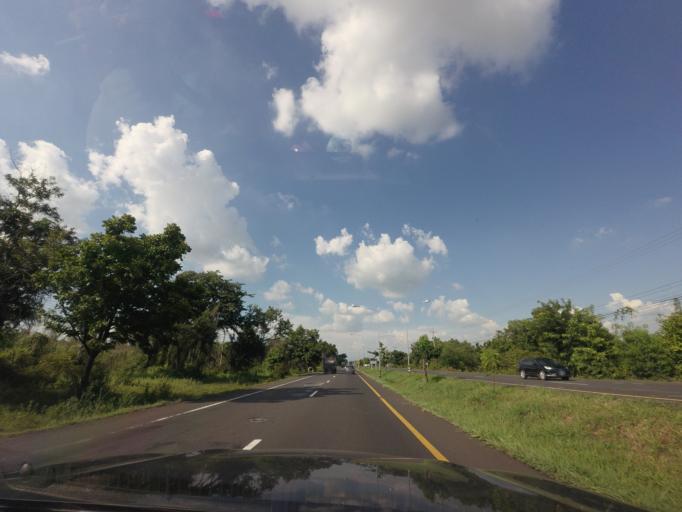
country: TH
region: Nakhon Ratchasima
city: Bua Lai
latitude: 15.7009
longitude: 102.5841
